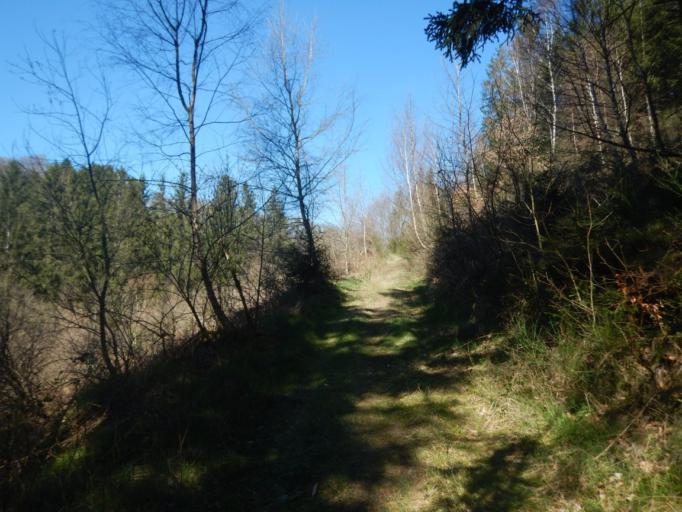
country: LU
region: Diekirch
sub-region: Canton de Clervaux
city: Weiswampach
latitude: 50.1065
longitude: 6.0435
